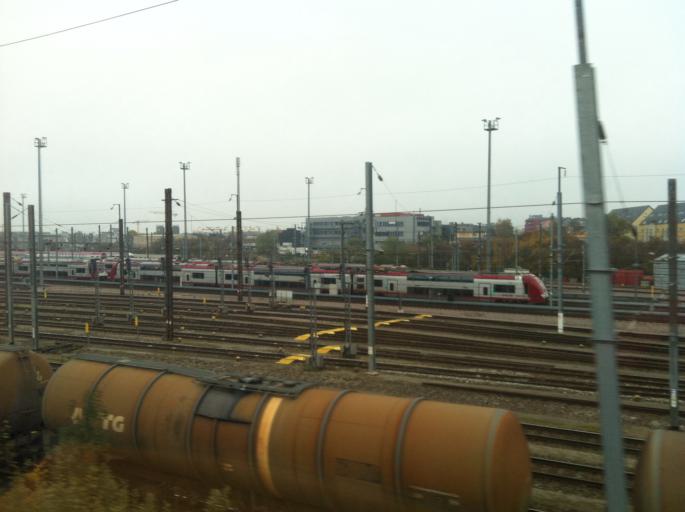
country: LU
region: Luxembourg
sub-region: Canton de Luxembourg
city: Hesperange
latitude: 49.5871
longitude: 6.1354
